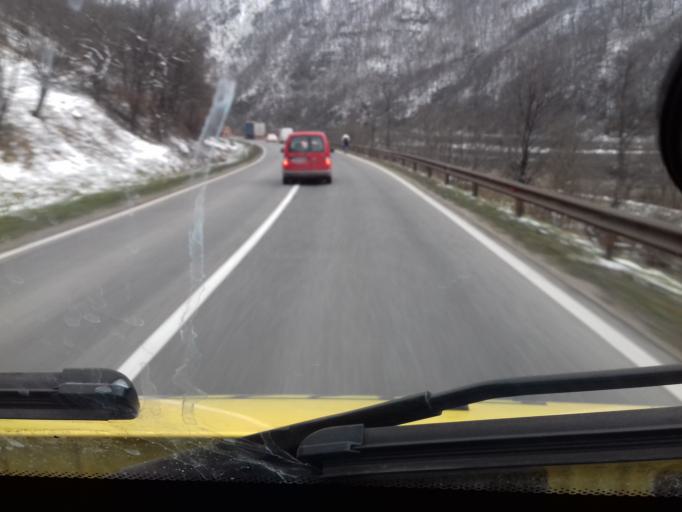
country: BA
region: Federation of Bosnia and Herzegovina
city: Zeljezno Polje
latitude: 44.3116
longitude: 17.9028
